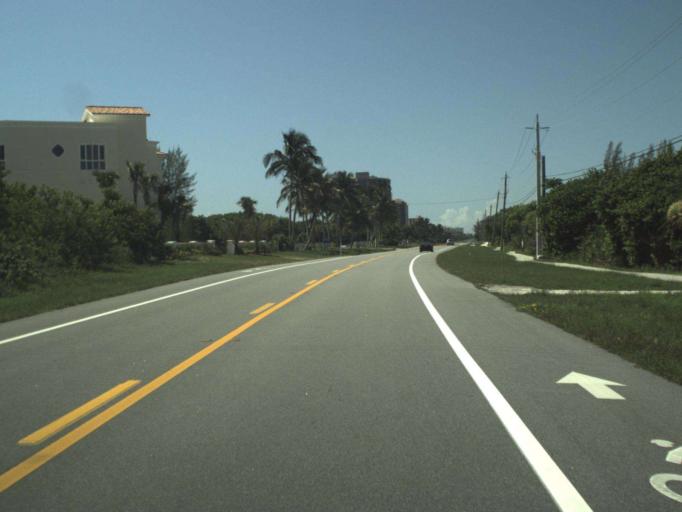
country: US
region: Florida
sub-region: Saint Lucie County
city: Fort Pierce North
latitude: 27.5189
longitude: -80.3099
